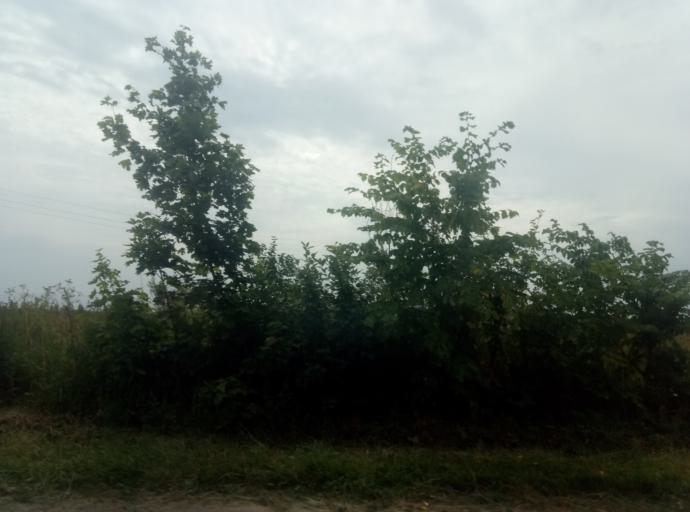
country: RU
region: Tula
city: Zhdankovskiy
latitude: 53.7742
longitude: 38.1575
